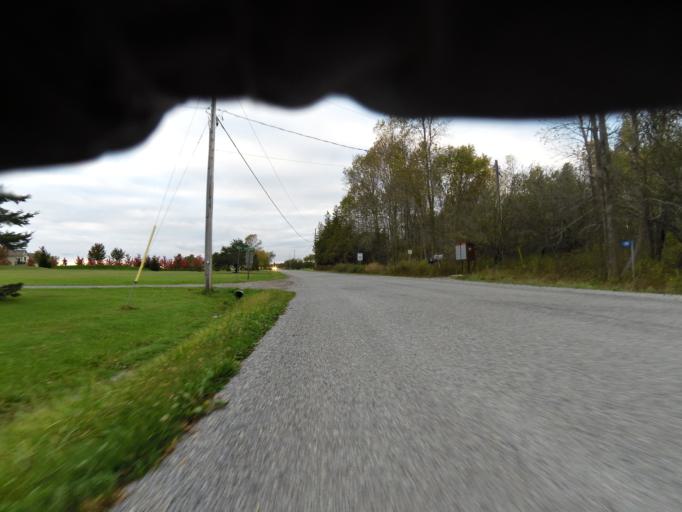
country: CA
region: Ontario
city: Quinte West
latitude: 44.0115
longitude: -77.7770
